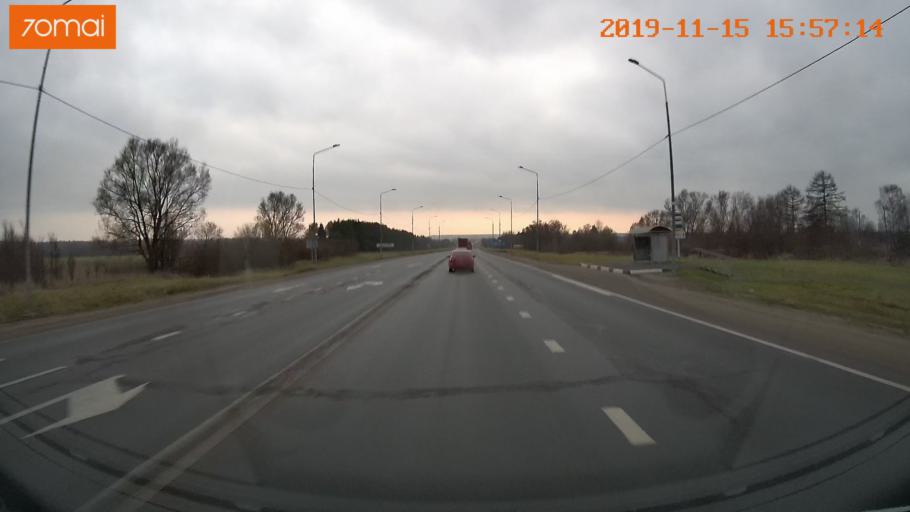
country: RU
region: Jaroslavl
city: Yaroslavl
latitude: 57.8325
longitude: 39.9654
